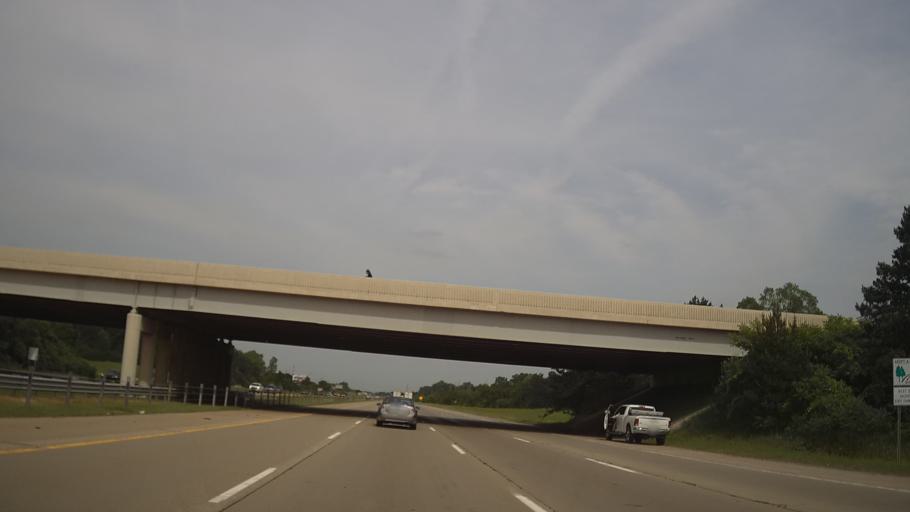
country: US
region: Michigan
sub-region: Wayne County
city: Belleville
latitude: 42.2198
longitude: -83.4857
